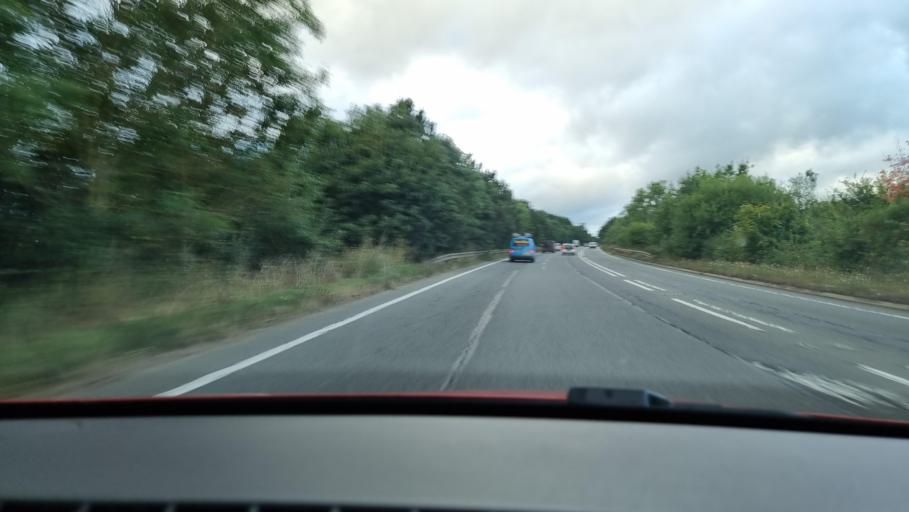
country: GB
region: England
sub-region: Central Bedfordshire
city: Leighton Buzzard
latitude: 51.9015
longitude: -0.6810
